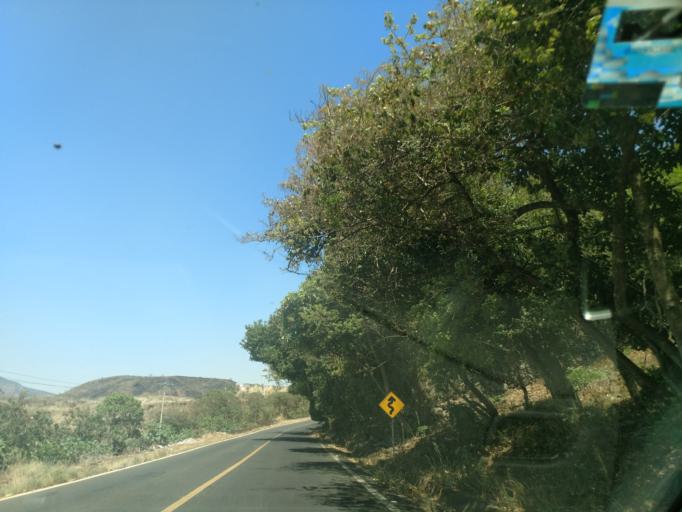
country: MX
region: Nayarit
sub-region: Tepic
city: La Corregidora
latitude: 21.5015
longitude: -104.7666
